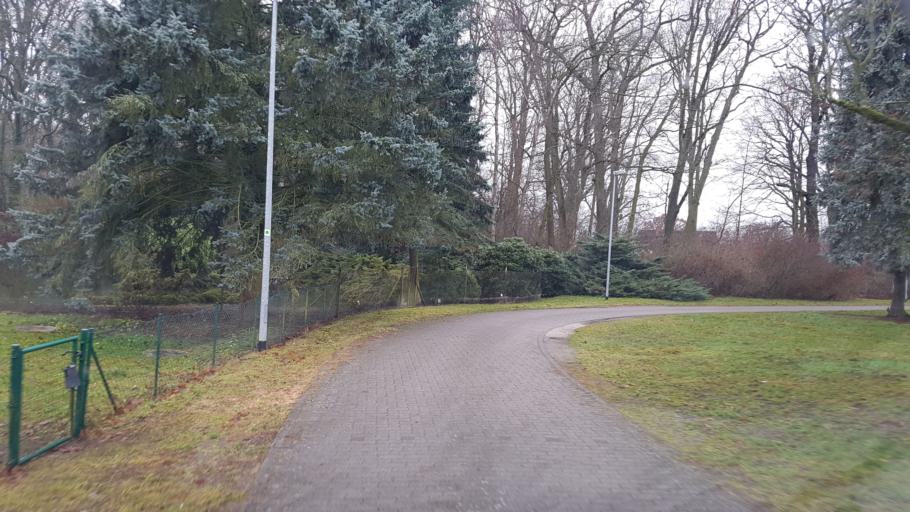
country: DE
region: Brandenburg
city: Altdobern
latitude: 51.6905
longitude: 14.0051
